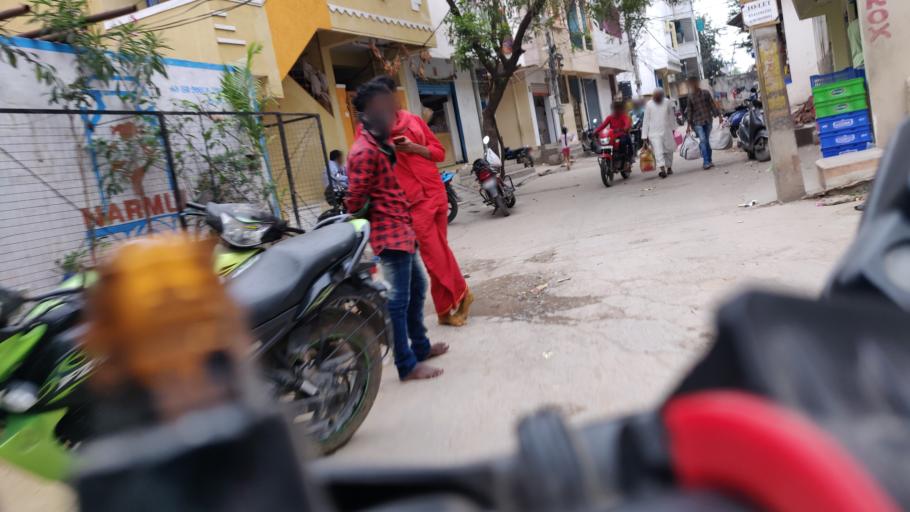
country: IN
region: Telangana
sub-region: Rangareddi
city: Kukatpalli
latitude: 17.4503
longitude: 78.4104
